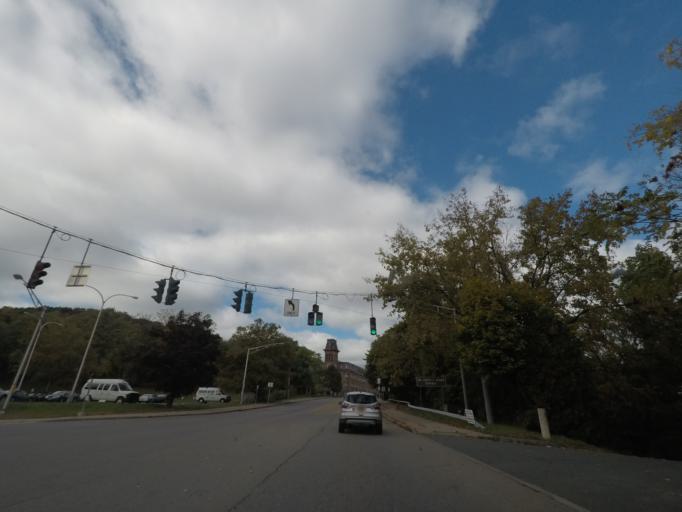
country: US
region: New York
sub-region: Albany County
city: Cohoes
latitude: 42.7774
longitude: -73.7006
